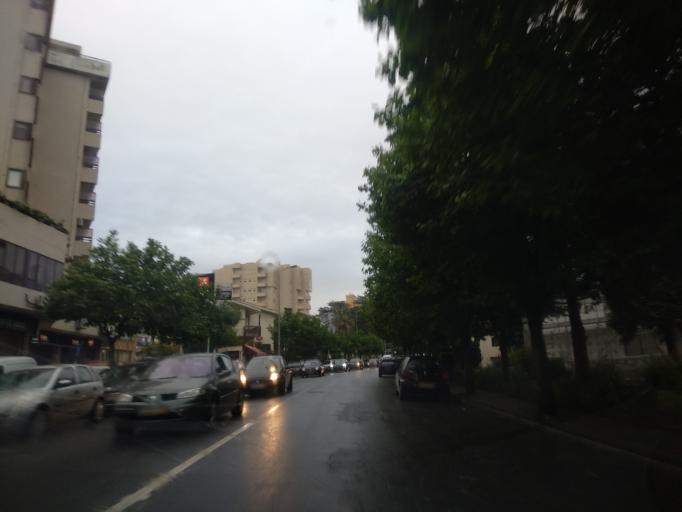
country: PT
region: Porto
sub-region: Gondomar
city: Rio Tinto
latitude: 41.1769
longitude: -8.5589
